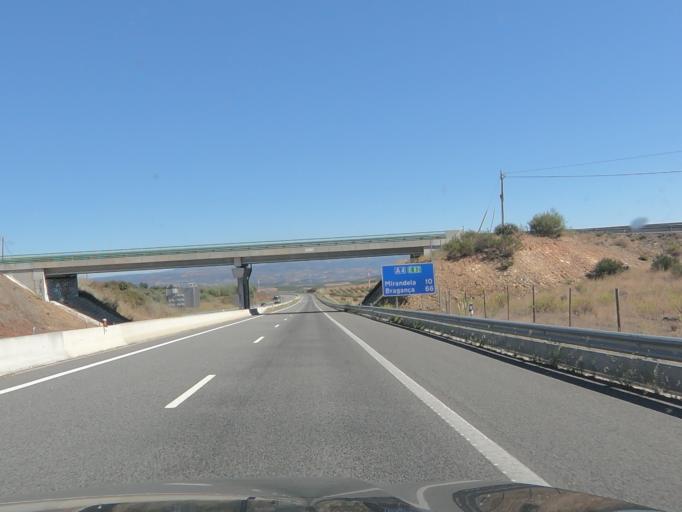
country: PT
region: Braganca
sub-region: Mirandela
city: Mirandela
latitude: 41.4509
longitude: -7.2812
